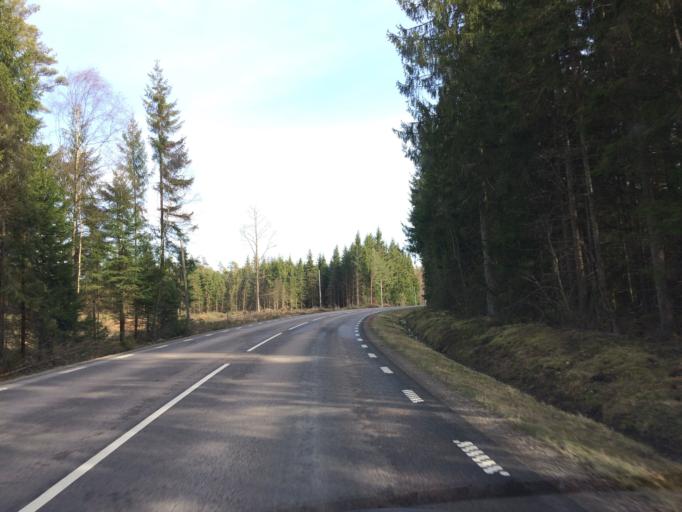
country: SE
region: Halland
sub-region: Hylte Kommun
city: Hyltebruk
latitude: 57.0218
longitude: 13.1916
